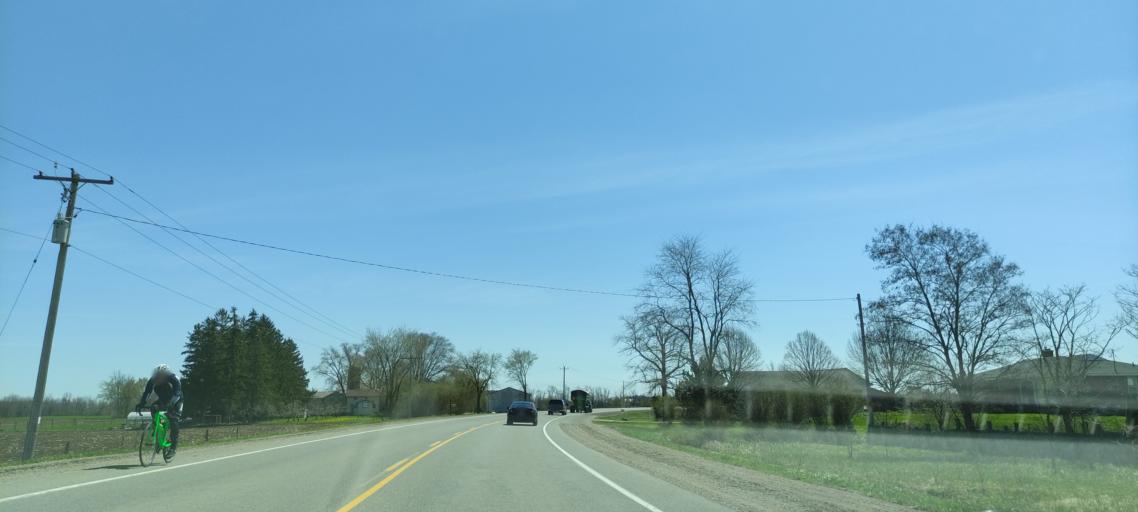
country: CA
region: Ontario
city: Waterloo
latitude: 43.5810
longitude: -80.4189
